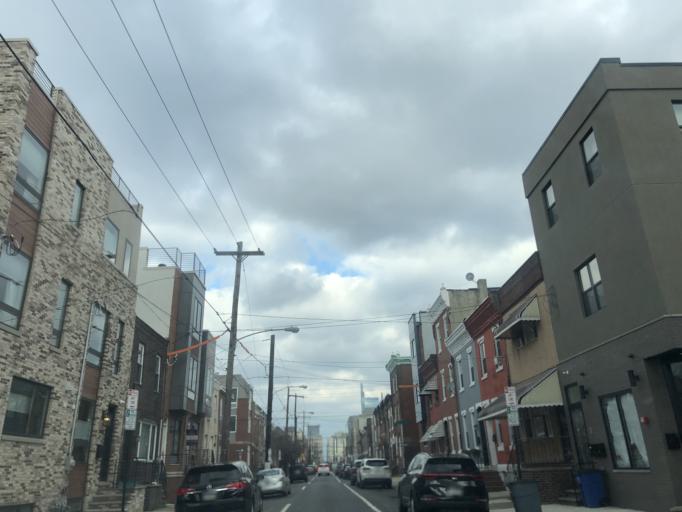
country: US
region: Pennsylvania
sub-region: Philadelphia County
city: Philadelphia
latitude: 39.9329
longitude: -75.1777
